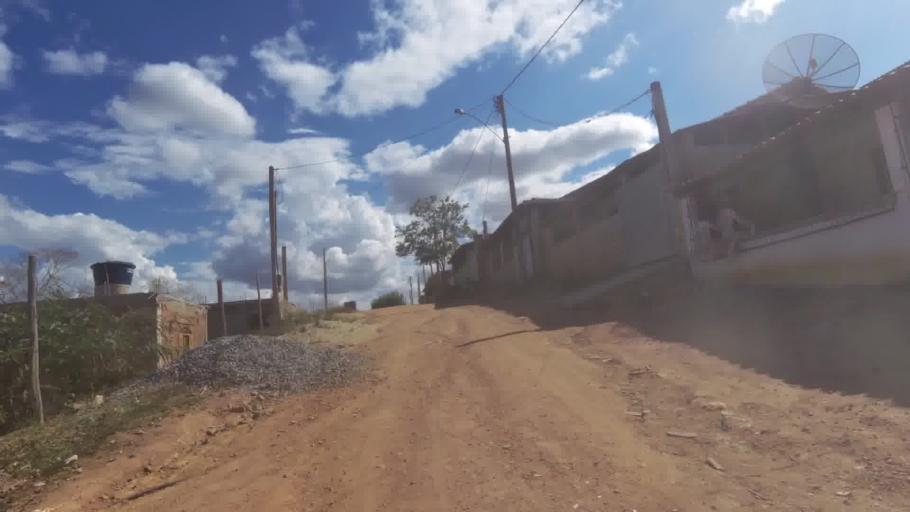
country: BR
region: Espirito Santo
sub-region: Cachoeiro De Itapemirim
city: Cachoeiro de Itapemirim
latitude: -20.9209
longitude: -41.1947
